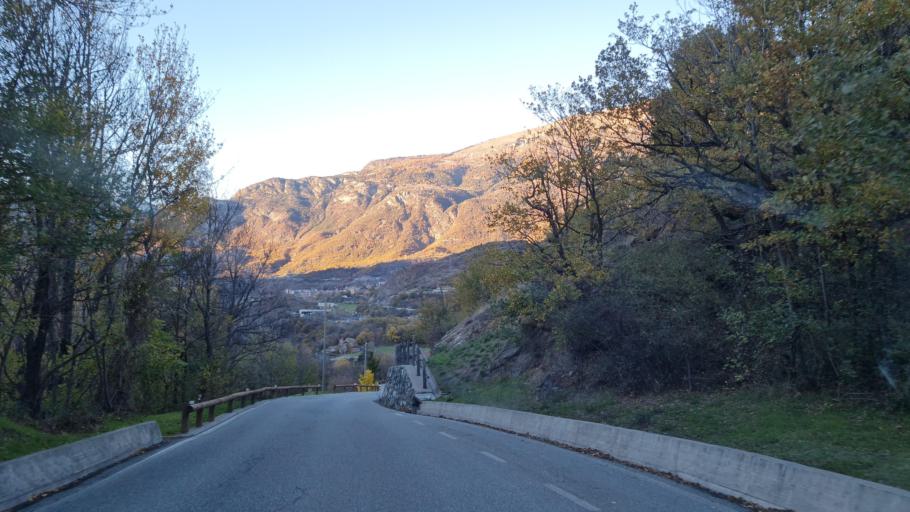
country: IT
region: Aosta Valley
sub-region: Valle d'Aosta
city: Montjovet
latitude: 45.7279
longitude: 7.6678
